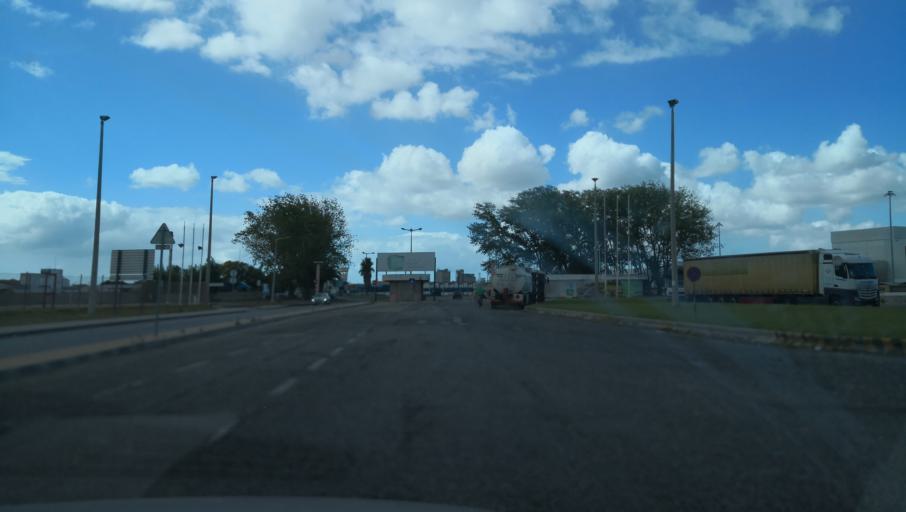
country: PT
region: Setubal
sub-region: Barreiro
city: Barreiro
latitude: 38.6670
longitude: -9.0572
